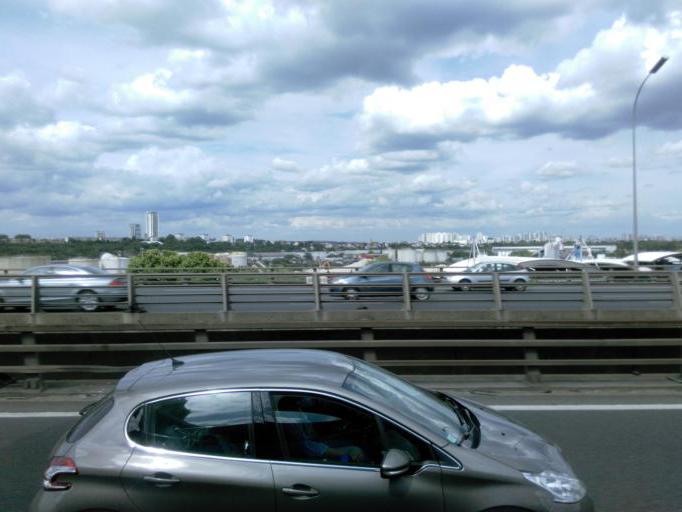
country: FR
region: Ile-de-France
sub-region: Departement des Hauts-de-Seine
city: Gennevilliers
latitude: 48.9438
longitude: 2.2870
